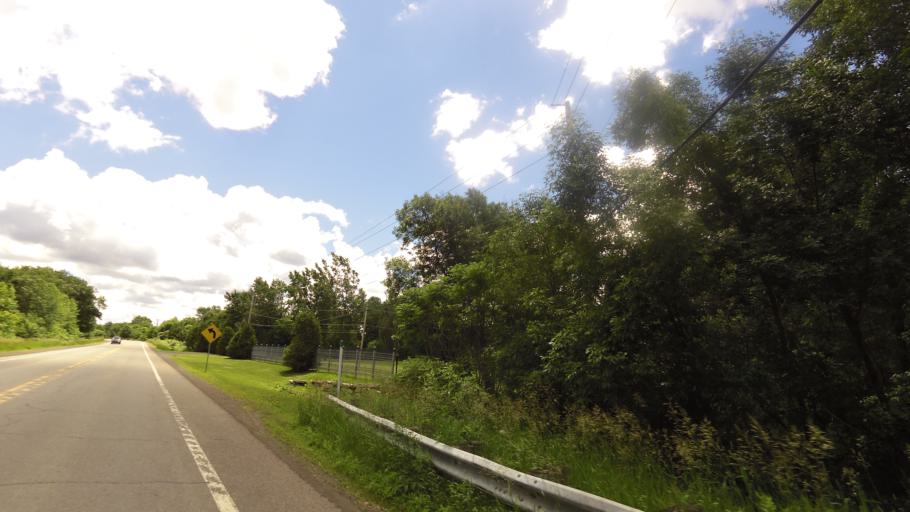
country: CA
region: Quebec
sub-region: Monteregie
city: Rigaud
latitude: 45.5279
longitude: -74.2258
